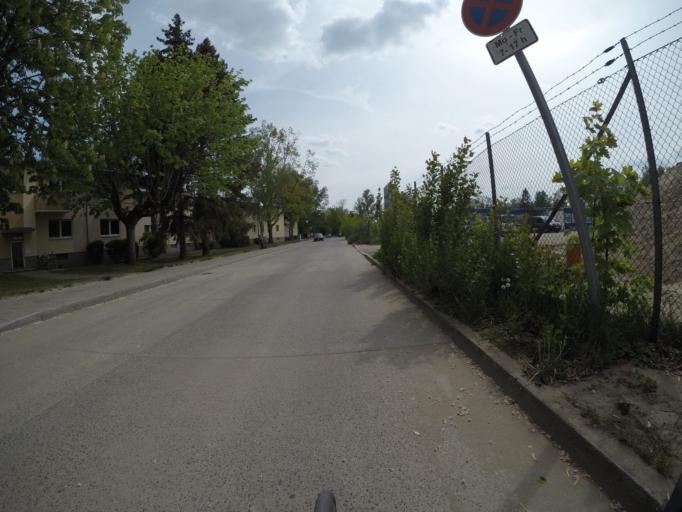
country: DE
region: Berlin
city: Lichtenrade
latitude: 52.3950
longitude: 13.3937
